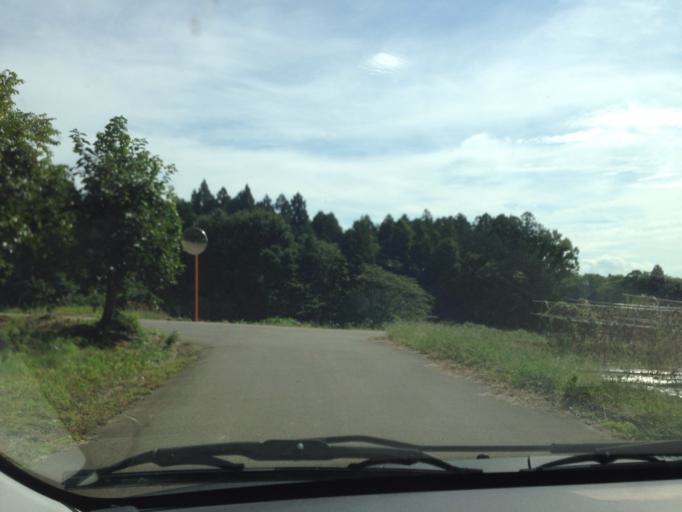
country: JP
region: Fukushima
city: Kitakata
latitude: 37.6173
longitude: 139.9329
